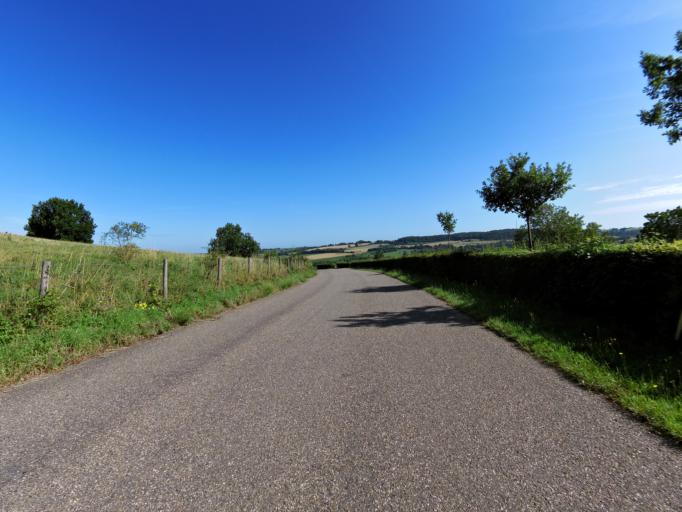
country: NL
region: Limburg
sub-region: Valkenburg aan de Geul
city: Schin op Geul
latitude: 50.8133
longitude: 5.9013
